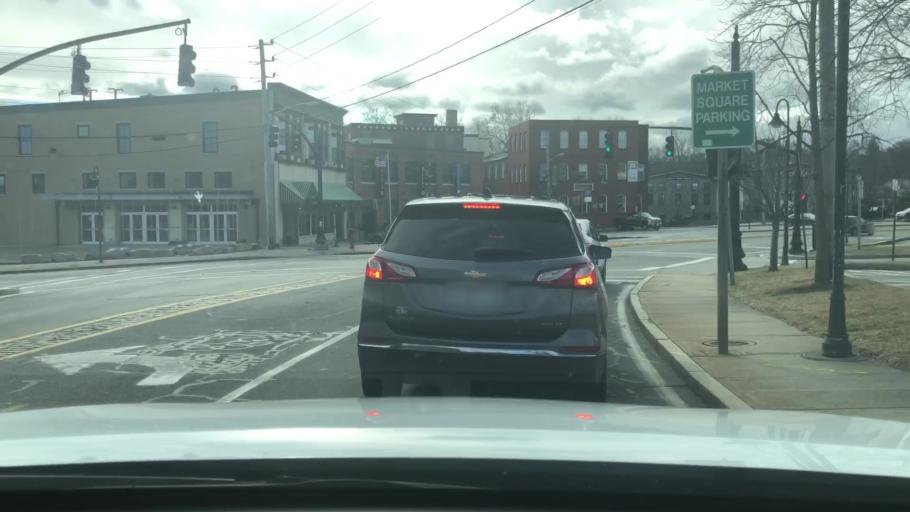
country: US
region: Rhode Island
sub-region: Providence County
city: Woonsocket
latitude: 42.0001
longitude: -71.5162
